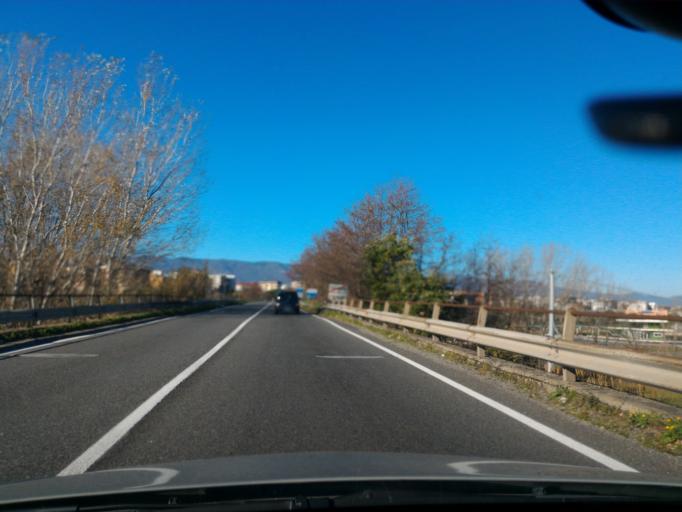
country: IT
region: Calabria
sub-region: Provincia di Cosenza
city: Quattromiglia
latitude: 39.3281
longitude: 16.2526
